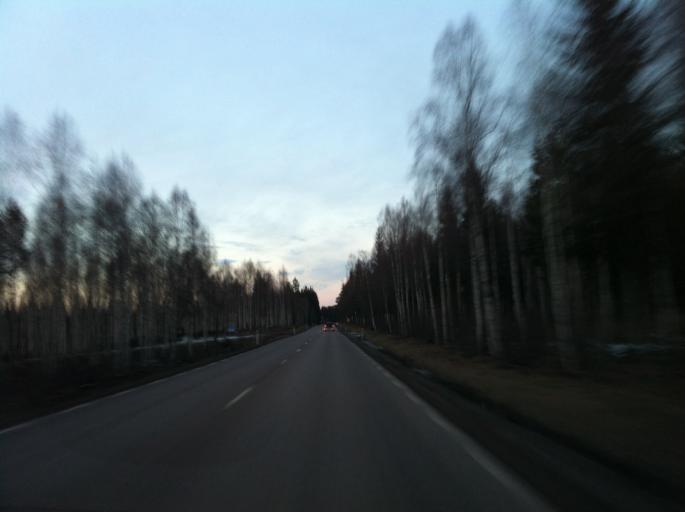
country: SE
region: Dalarna
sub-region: Orsa Kommun
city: Orsa
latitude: 61.0631
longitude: 14.6127
